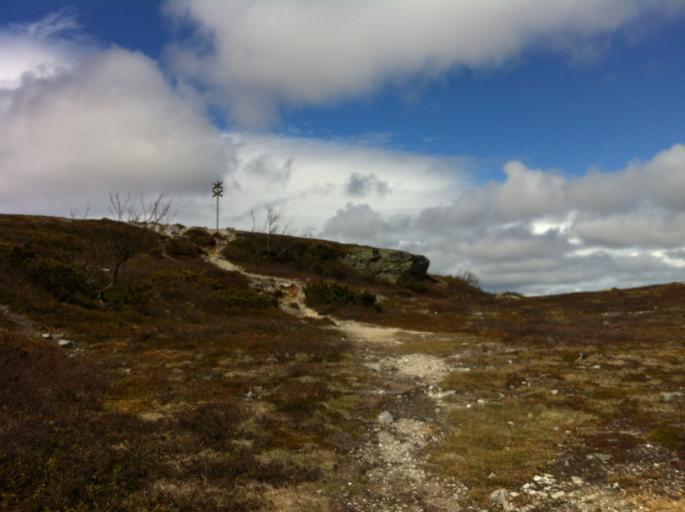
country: SE
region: Jaemtland
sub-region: Are Kommun
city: Are
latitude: 62.6858
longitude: 12.9658
